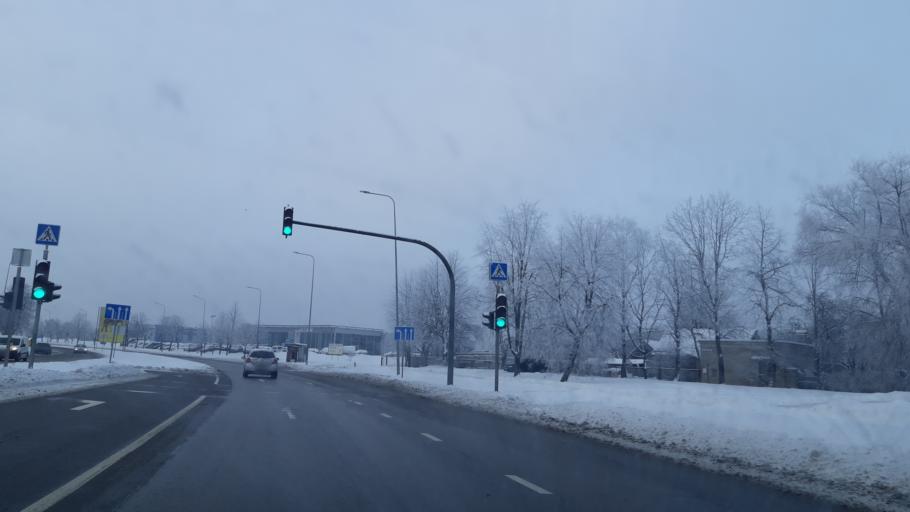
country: LT
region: Kauno apskritis
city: Dainava (Kaunas)
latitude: 54.9296
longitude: 23.9705
